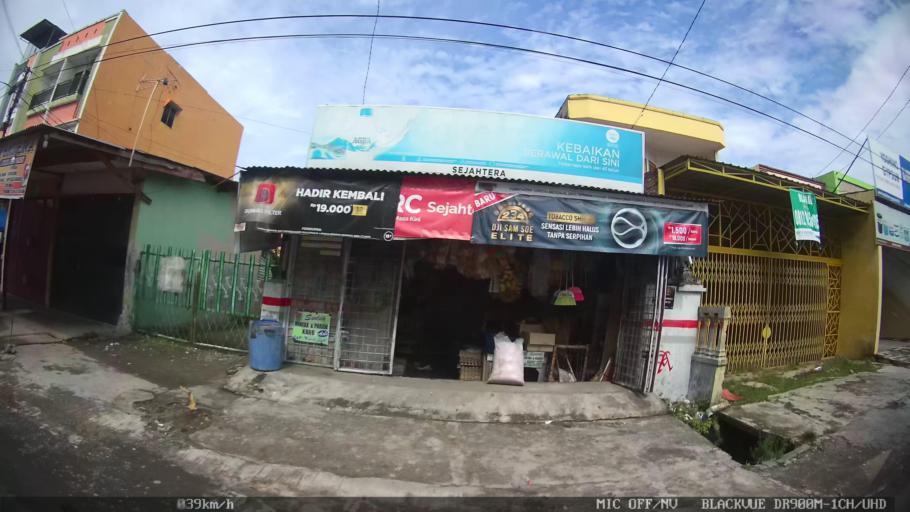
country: ID
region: North Sumatra
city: Medan
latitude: 3.6141
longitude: 98.6453
